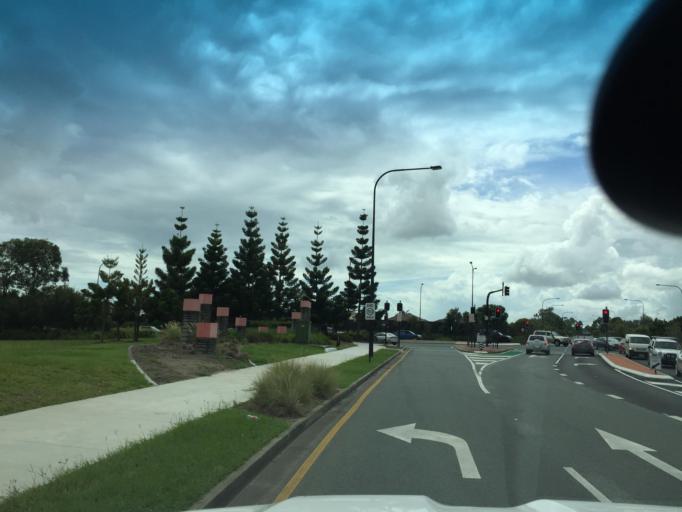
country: AU
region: Queensland
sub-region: Moreton Bay
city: Deception Bay
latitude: -27.2144
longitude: 152.9990
